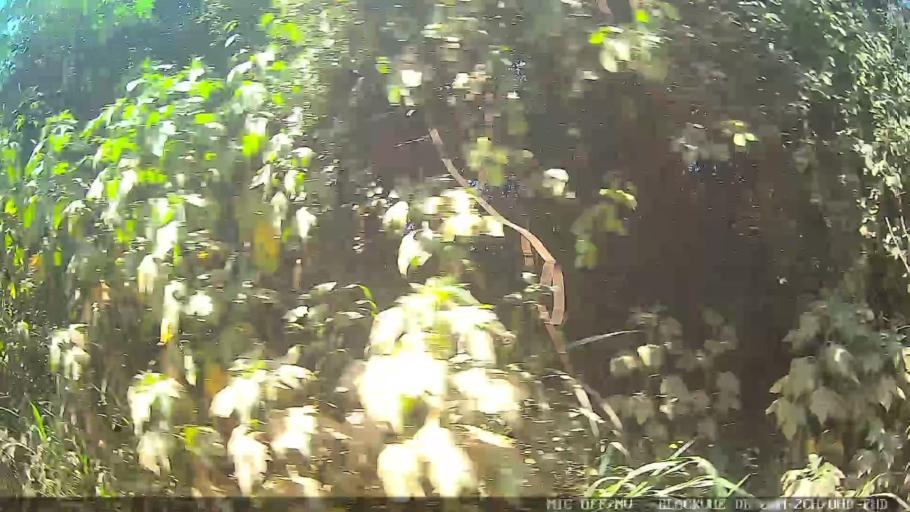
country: BR
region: Sao Paulo
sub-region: Jarinu
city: Jarinu
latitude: -23.0725
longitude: -46.6610
